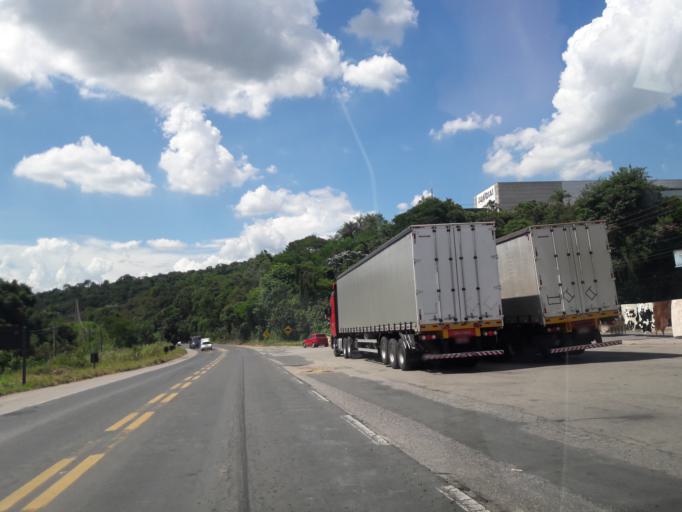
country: BR
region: Sao Paulo
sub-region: Campo Limpo Paulista
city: Campo Limpo Paulista
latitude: -23.2271
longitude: -46.7889
